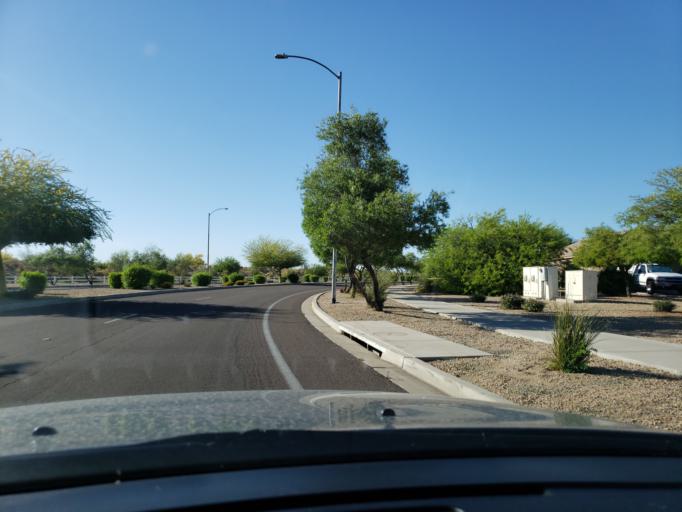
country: US
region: Arizona
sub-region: Maricopa County
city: Youngtown
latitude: 33.5684
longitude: -112.3108
